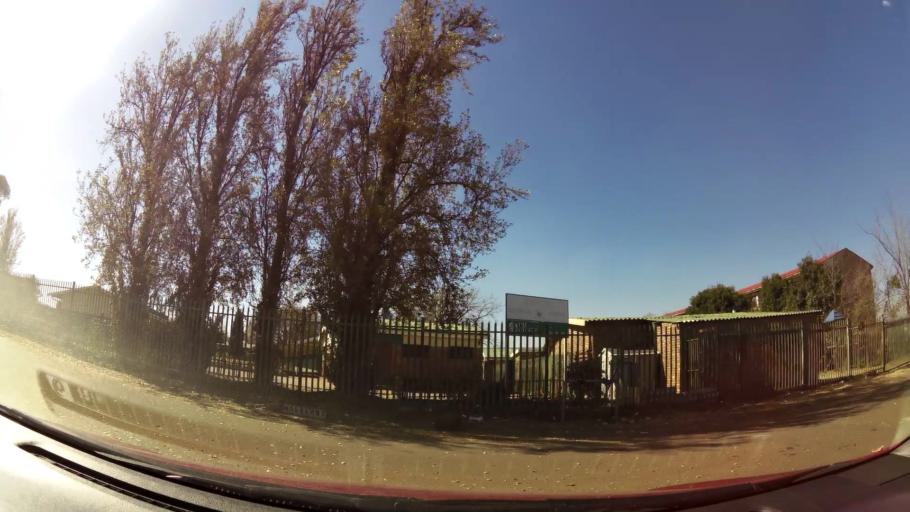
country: ZA
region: Gauteng
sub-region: City of Johannesburg Metropolitan Municipality
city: Soweto
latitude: -26.2393
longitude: 27.8430
